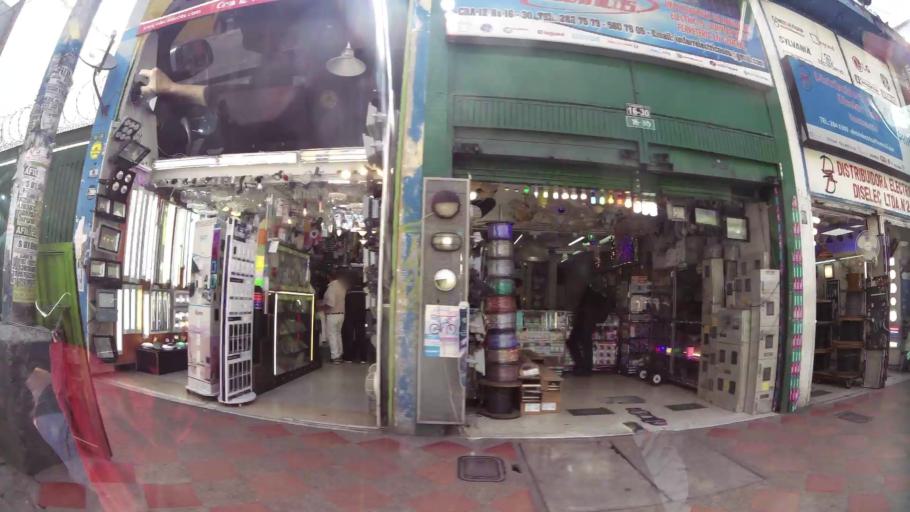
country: CO
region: Bogota D.C.
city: Bogota
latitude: 4.6051
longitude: -74.0760
